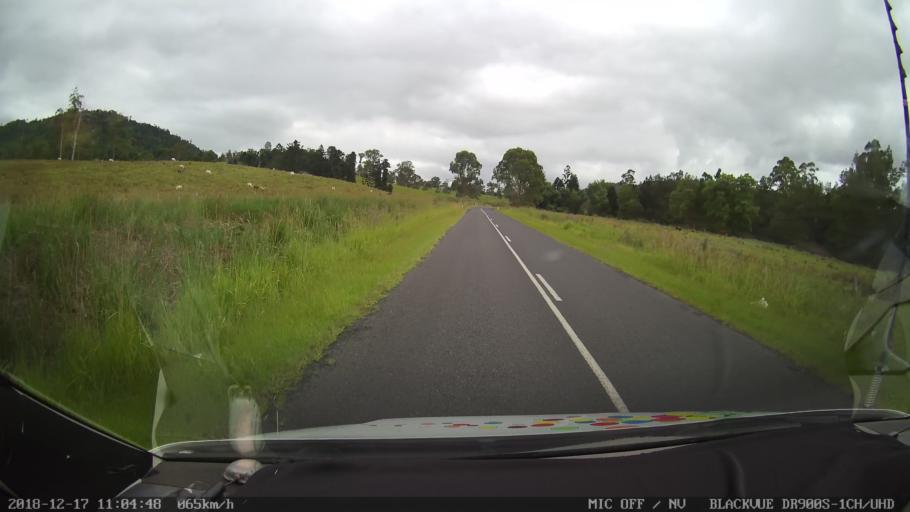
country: AU
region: New South Wales
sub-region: Kyogle
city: Kyogle
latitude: -28.7952
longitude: 152.6437
